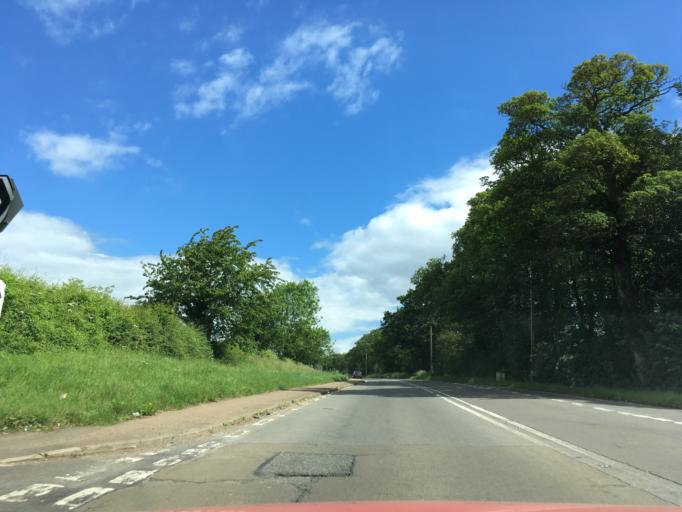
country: GB
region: England
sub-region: Oxfordshire
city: Bloxham
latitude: 52.0399
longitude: -1.3615
